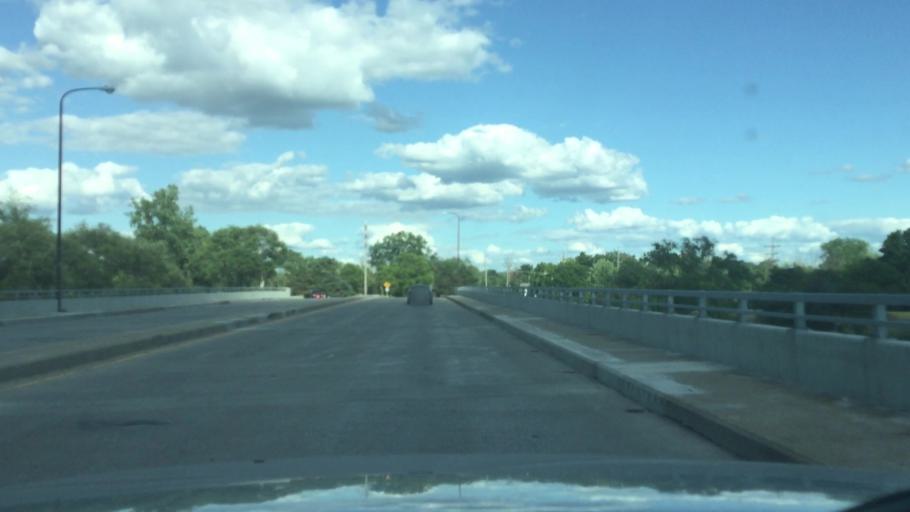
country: US
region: Michigan
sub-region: Saginaw County
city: Saginaw
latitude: 43.4016
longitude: -83.9660
